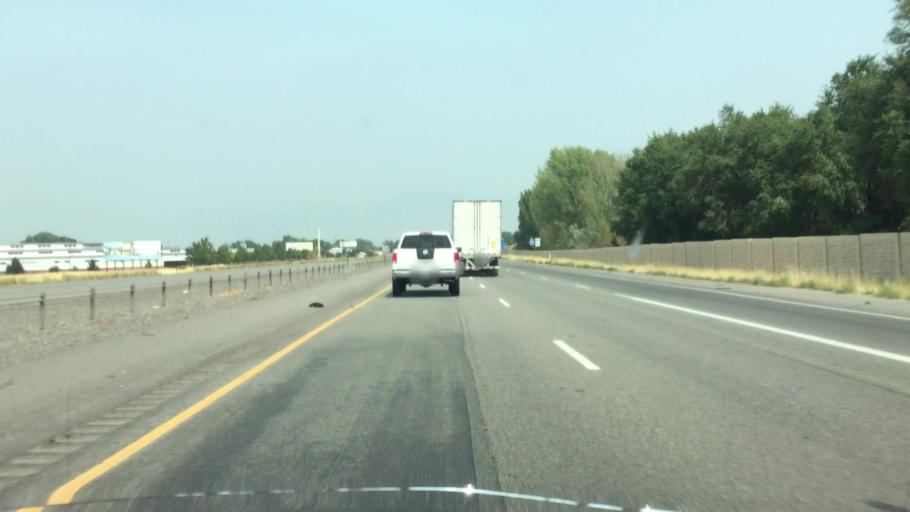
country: US
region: Utah
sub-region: Utah County
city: Payson
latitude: 40.0370
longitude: -111.7514
